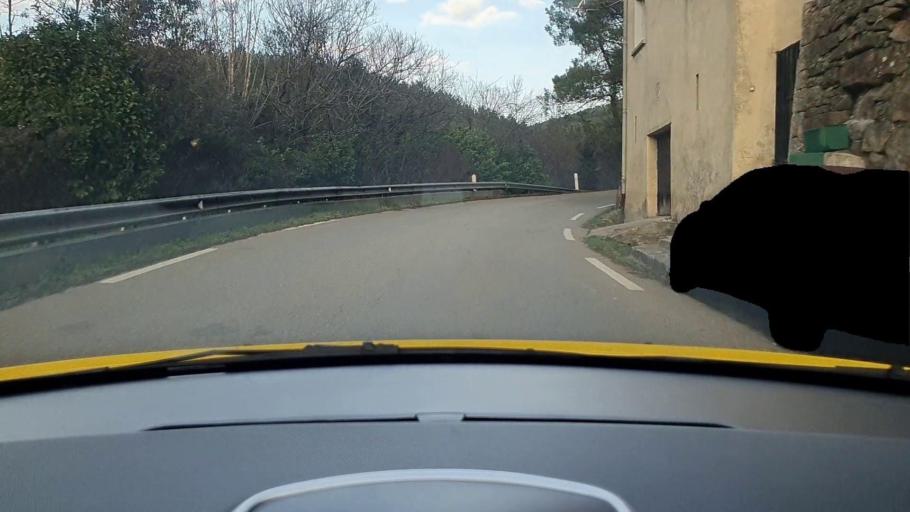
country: FR
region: Languedoc-Roussillon
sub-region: Departement du Gard
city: Les Salles-du-Gardon
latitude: 44.2521
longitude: 4.0449
